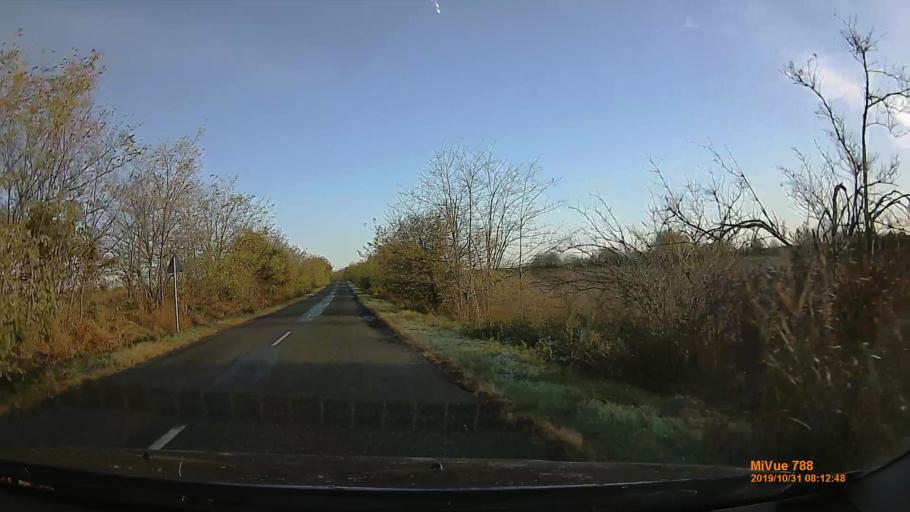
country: HU
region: Pest
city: Pilis
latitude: 47.3289
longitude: 19.5677
